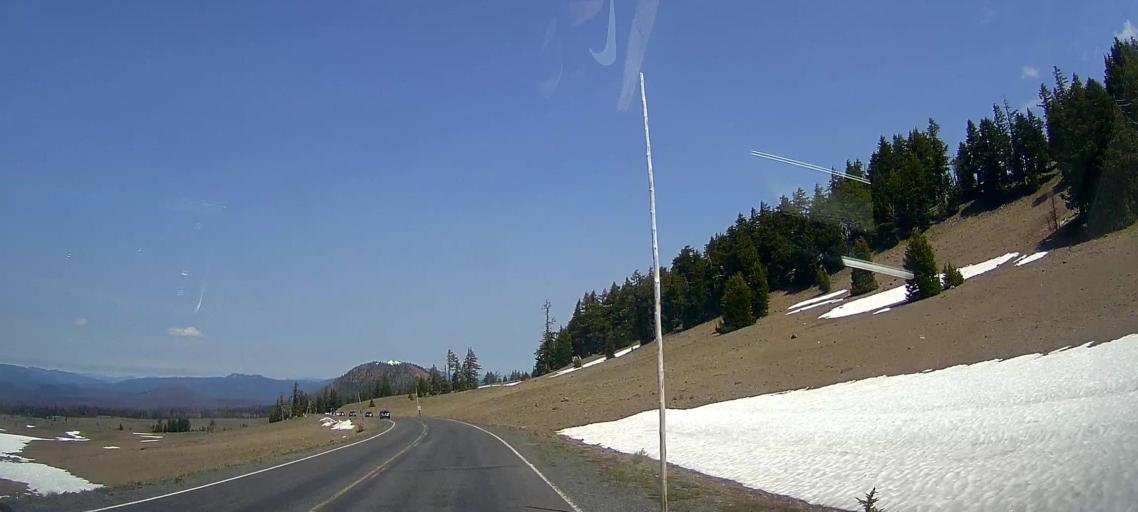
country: US
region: Oregon
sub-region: Jackson County
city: Shady Cove
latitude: 42.9677
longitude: -122.1513
